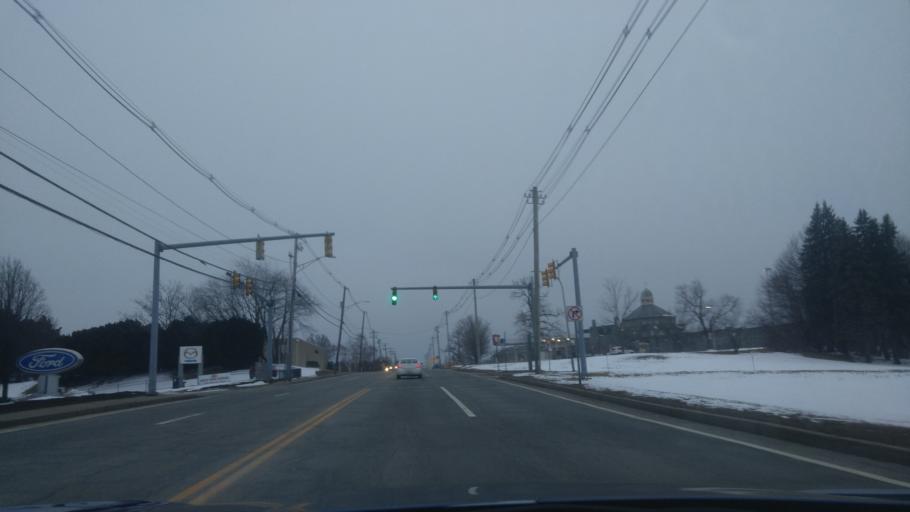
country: US
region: Rhode Island
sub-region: Providence County
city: Cranston
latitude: 41.7488
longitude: -71.4525
